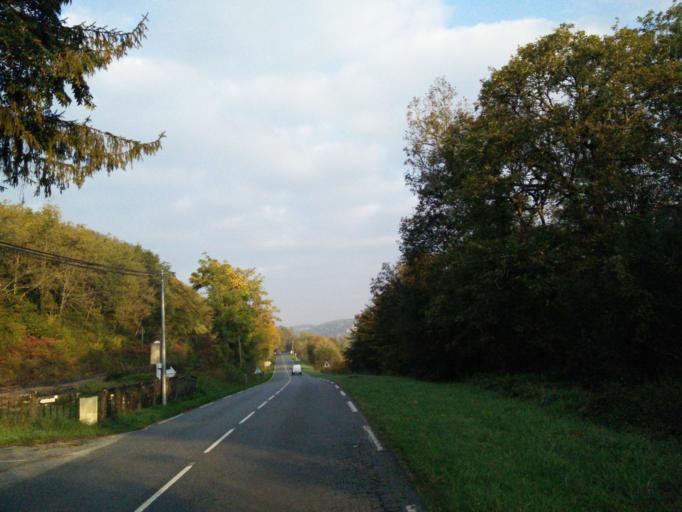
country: FR
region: Aquitaine
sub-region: Departement de la Dordogne
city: Le Bugue
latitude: 44.9782
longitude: 0.9564
